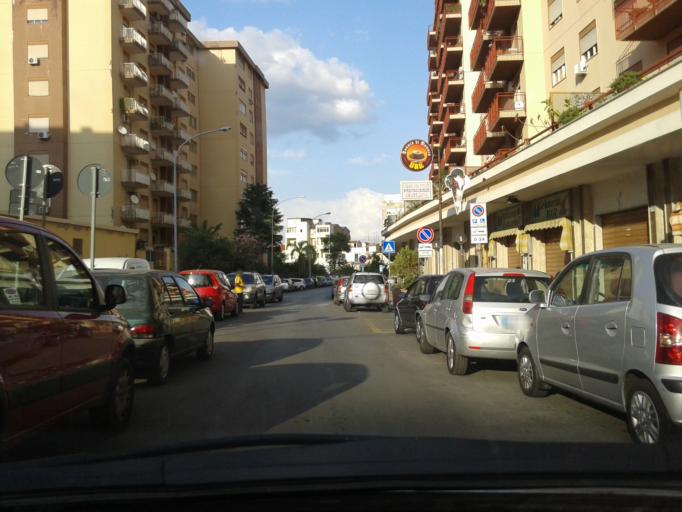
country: IT
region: Sicily
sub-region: Palermo
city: Palermo
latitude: 38.1071
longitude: 13.3380
